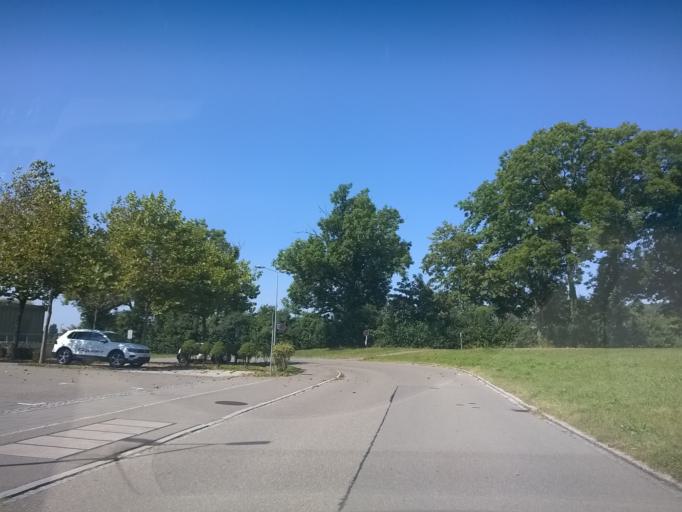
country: CH
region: Zurich
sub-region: Bezirk Buelach
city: Kloten / Freienberg (Chanzler-Chlini Chaseren)
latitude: 47.4626
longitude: 8.5785
